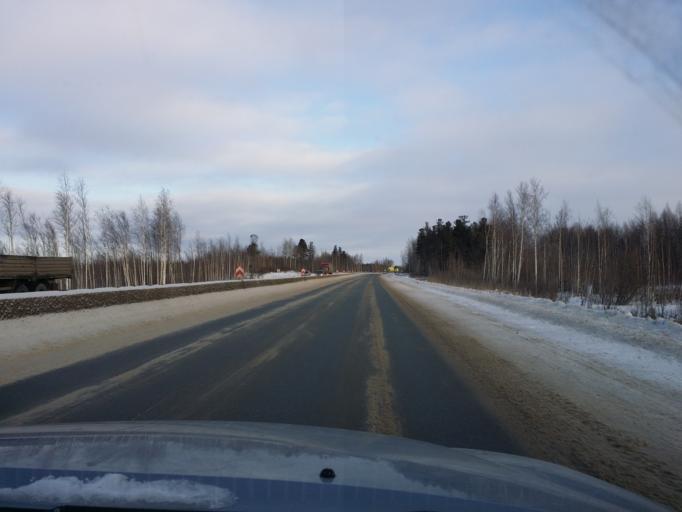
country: RU
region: Khanty-Mansiyskiy Avtonomnyy Okrug
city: Megion
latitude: 61.0618
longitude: 76.1760
